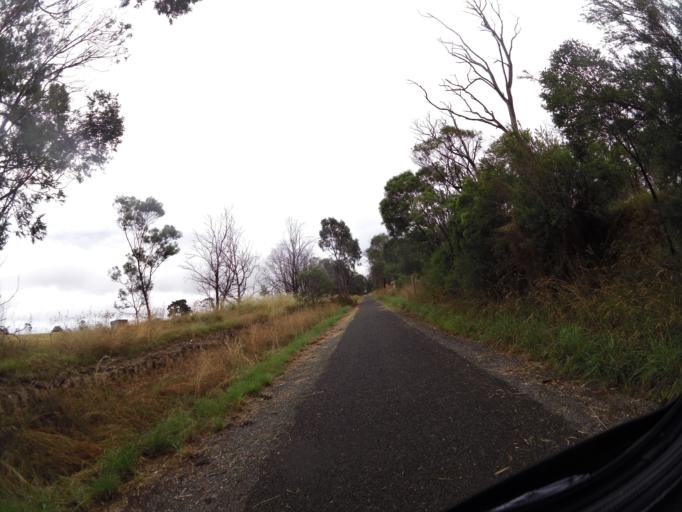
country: AU
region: Victoria
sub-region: East Gippsland
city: Bairnsdale
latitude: -37.8188
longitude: 147.7244
